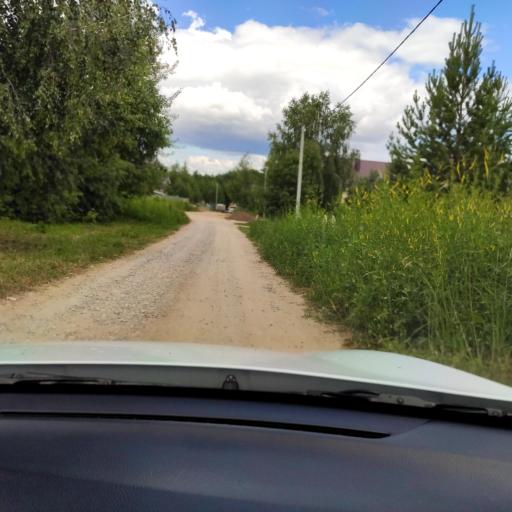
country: RU
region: Tatarstan
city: Vysokaya Gora
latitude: 55.7838
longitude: 49.2694
